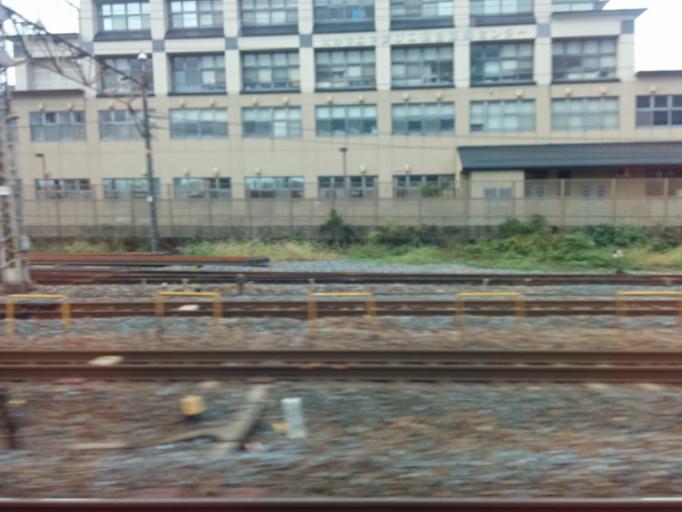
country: JP
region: Shiga Prefecture
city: Otsu-shi
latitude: 35.0006
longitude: 135.8787
